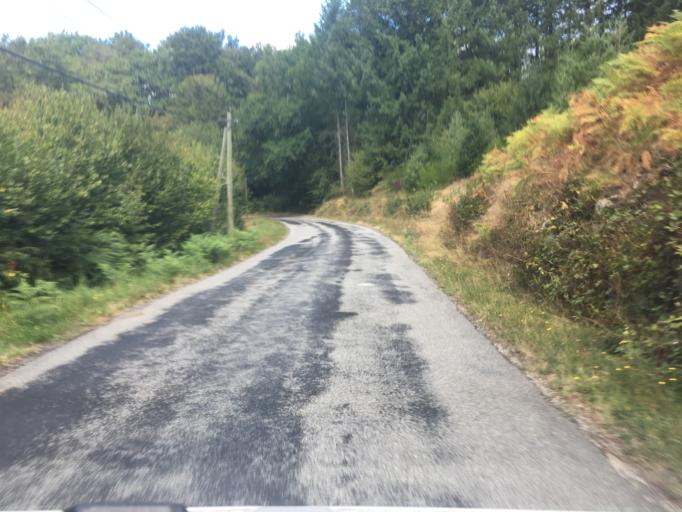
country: FR
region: Limousin
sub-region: Departement de la Correze
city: Neuvic
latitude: 45.4270
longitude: 2.3532
